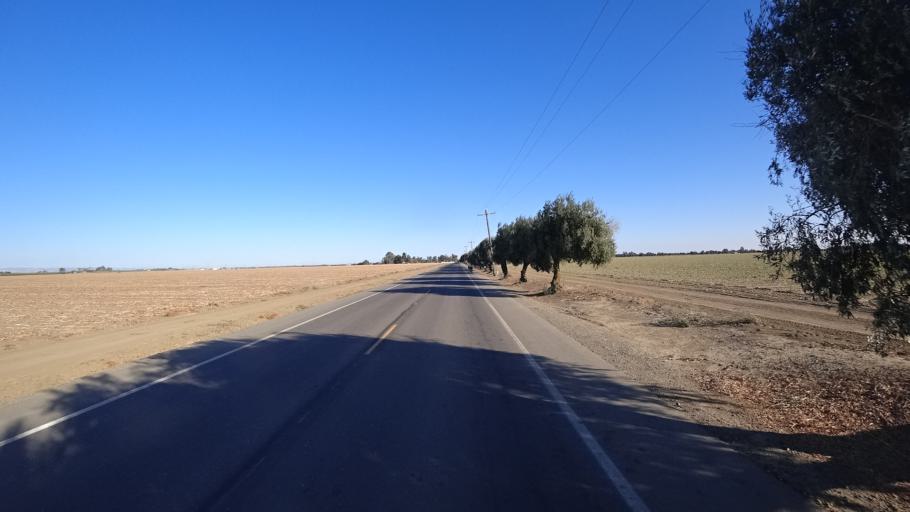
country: US
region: California
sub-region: Yolo County
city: Woodland
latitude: 38.6101
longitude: -121.7852
